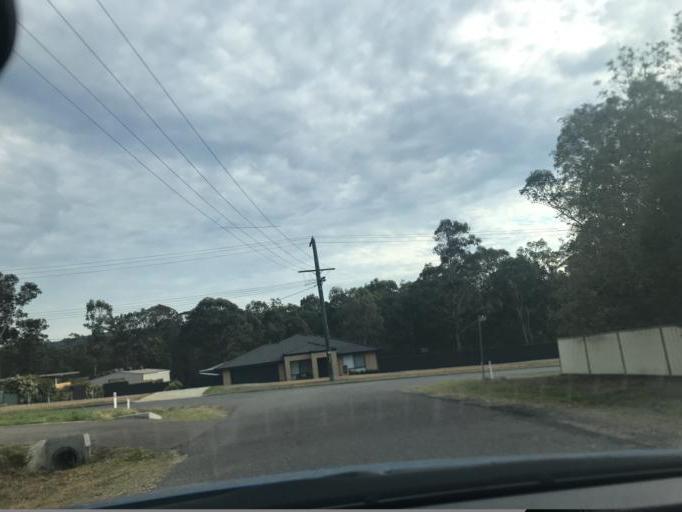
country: AU
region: New South Wales
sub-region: Cessnock
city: Cessnock
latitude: -32.9023
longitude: 151.2860
